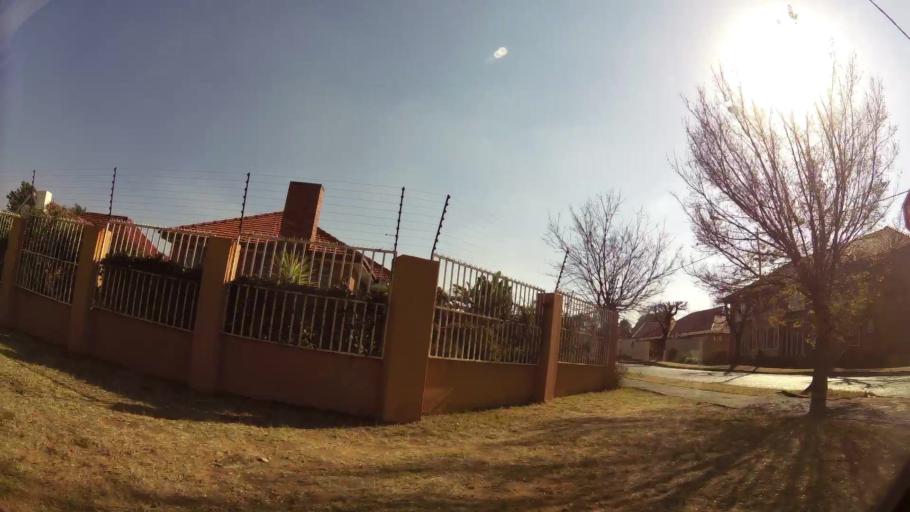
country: ZA
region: Gauteng
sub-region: City of Johannesburg Metropolitan Municipality
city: Johannesburg
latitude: -26.2582
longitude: 28.0666
